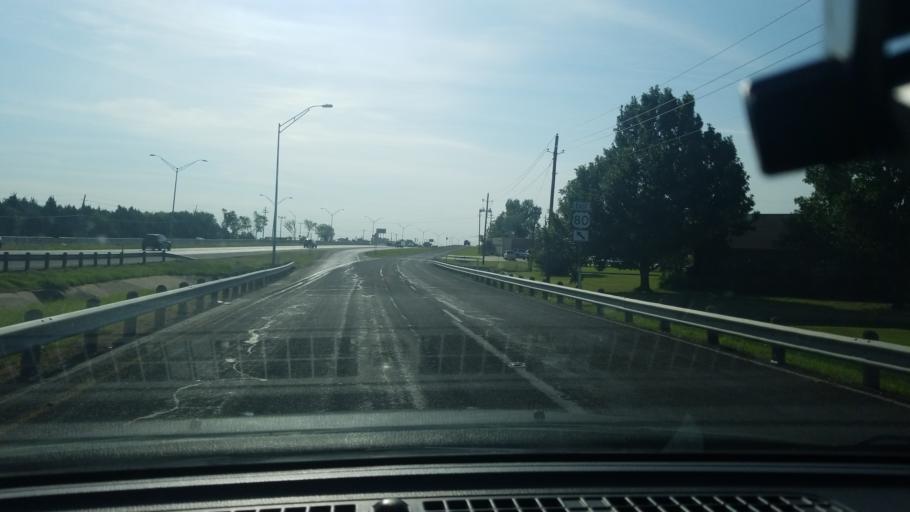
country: US
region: Texas
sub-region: Dallas County
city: Mesquite
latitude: 32.7923
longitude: -96.6081
